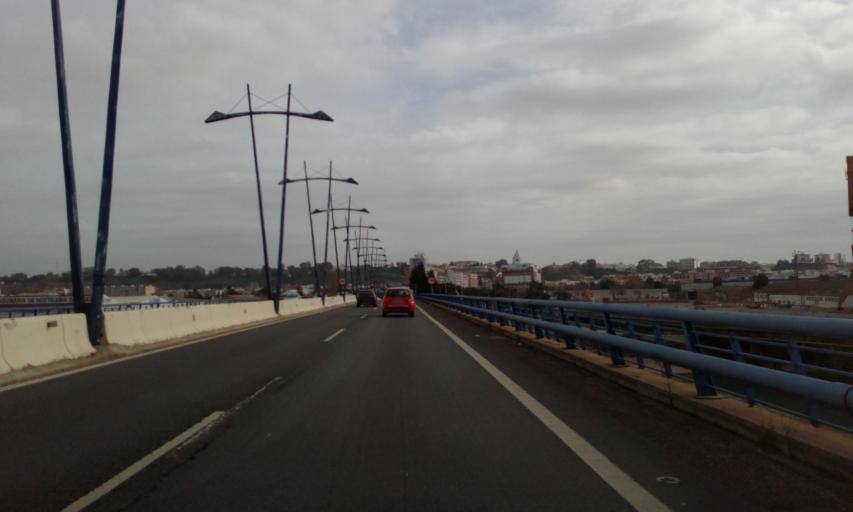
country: ES
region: Andalusia
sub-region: Provincia de Huelva
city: Huelva
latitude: 37.2675
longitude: -6.9643
